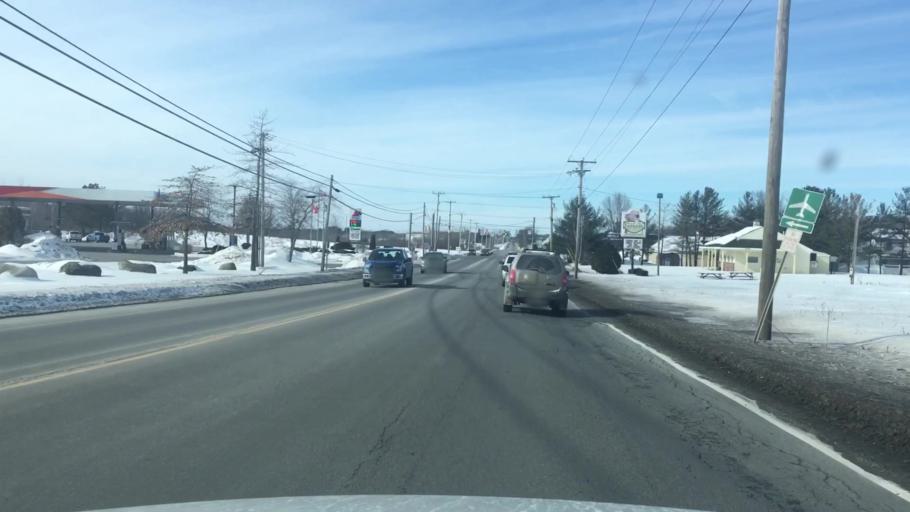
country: US
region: Maine
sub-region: Penobscot County
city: Bangor
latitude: 44.8349
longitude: -68.7902
